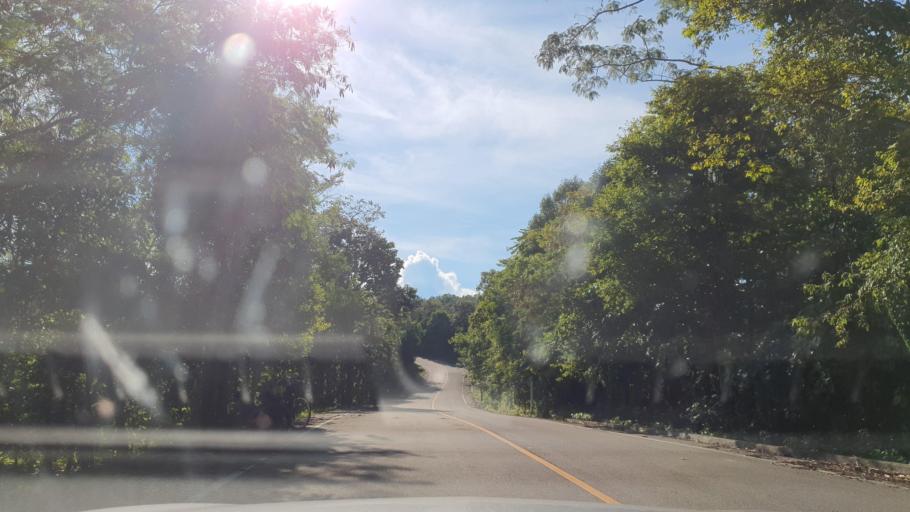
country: TH
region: Chiang Mai
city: Mae On
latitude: 18.7682
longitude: 99.2927
